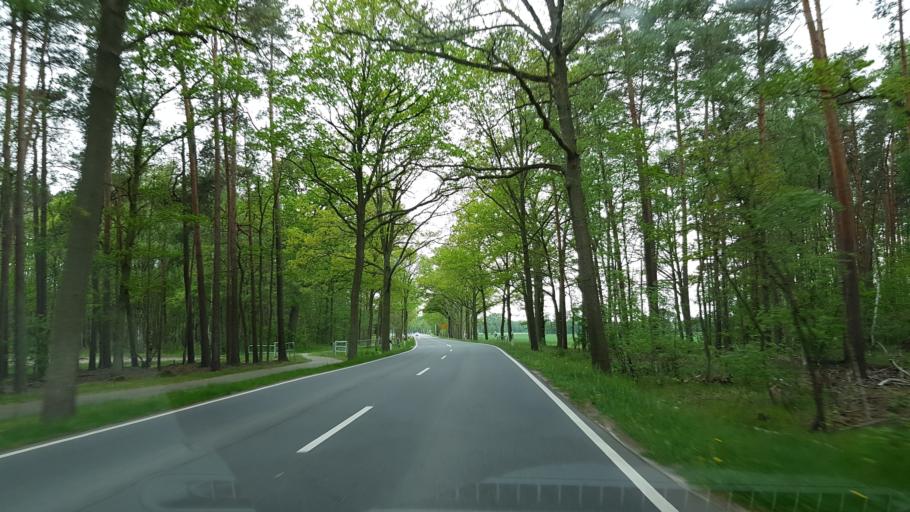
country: DE
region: Lower Saxony
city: Trebel
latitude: 52.9731
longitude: 11.2831
